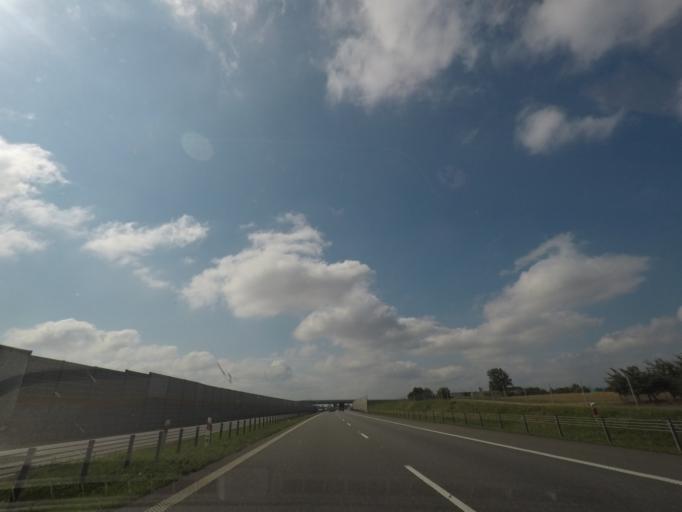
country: PL
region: Kujawsko-Pomorskie
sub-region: Powiat torunski
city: Lubicz Dolny
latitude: 53.0714
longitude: 18.7510
